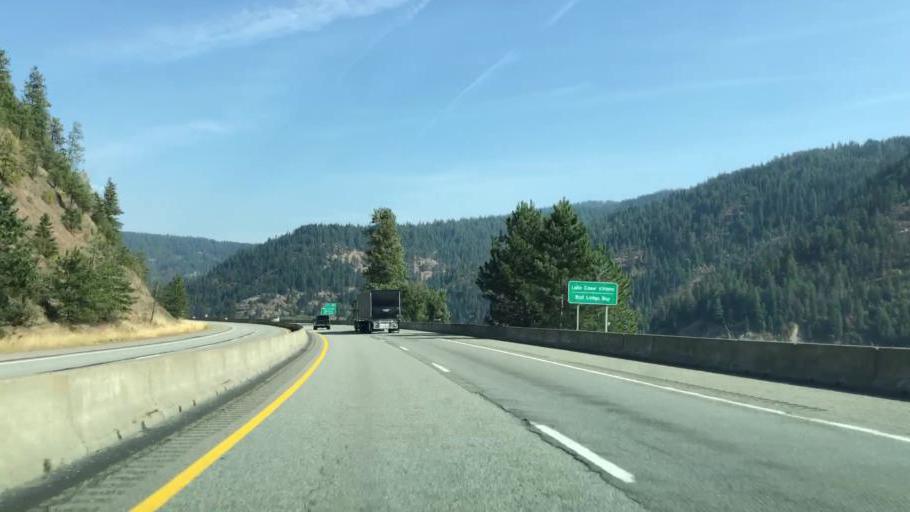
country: US
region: Idaho
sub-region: Kootenai County
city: Coeur d'Alene
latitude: 47.6241
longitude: -116.6659
